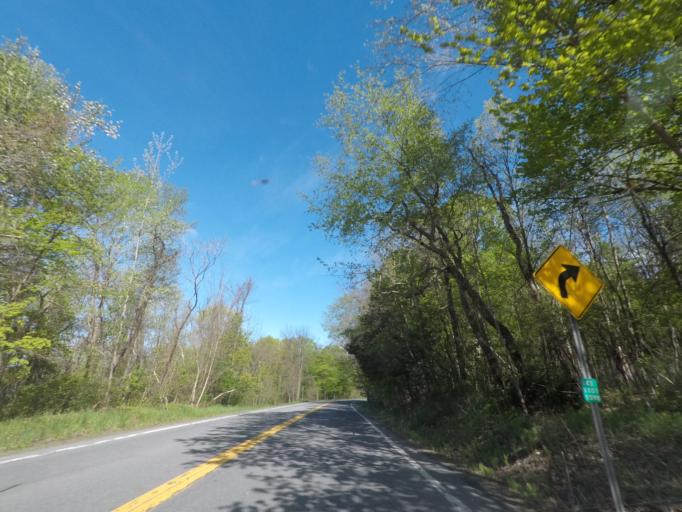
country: US
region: New York
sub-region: Albany County
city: Ravena
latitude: 42.4887
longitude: -73.9377
